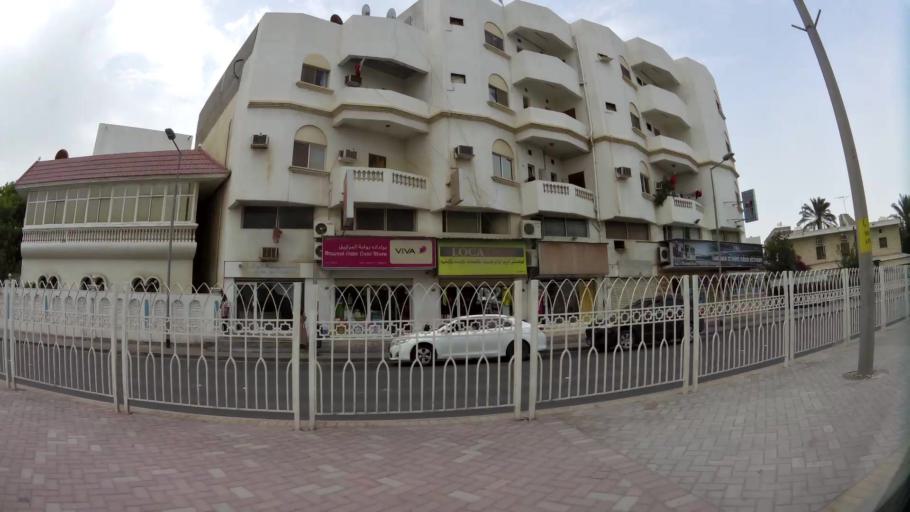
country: BH
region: Northern
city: Ar Rifa'
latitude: 26.1243
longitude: 50.5429
